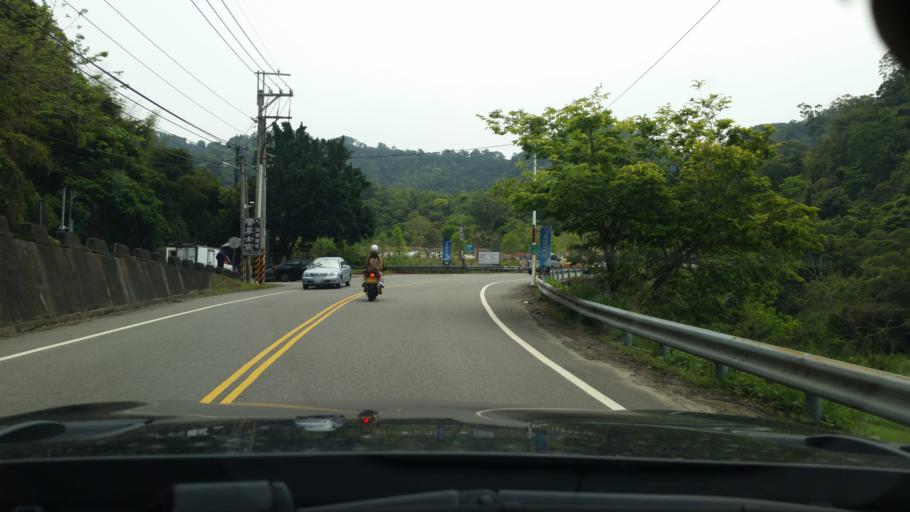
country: TW
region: Taiwan
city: Fengyuan
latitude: 24.3409
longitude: 120.7725
